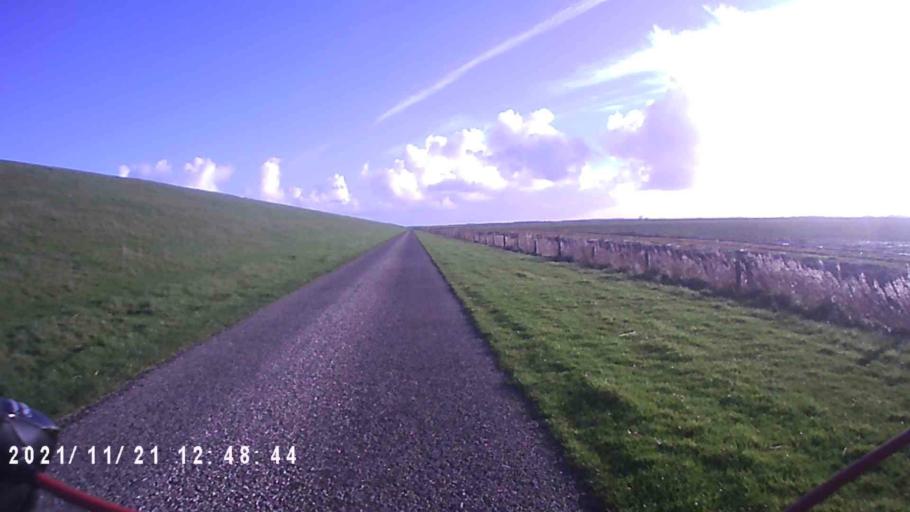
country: NL
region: Friesland
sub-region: Gemeente Dongeradeel
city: Anjum
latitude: 53.4006
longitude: 6.1113
